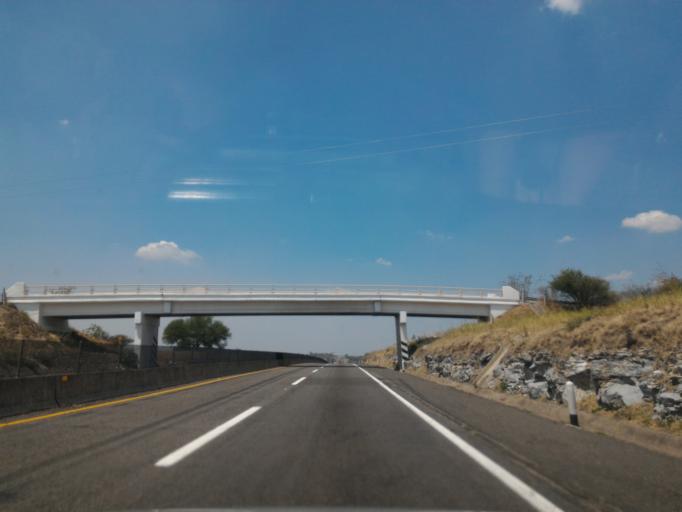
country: MX
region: Jalisco
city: Jalostotitlan
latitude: 21.0951
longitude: -102.4810
